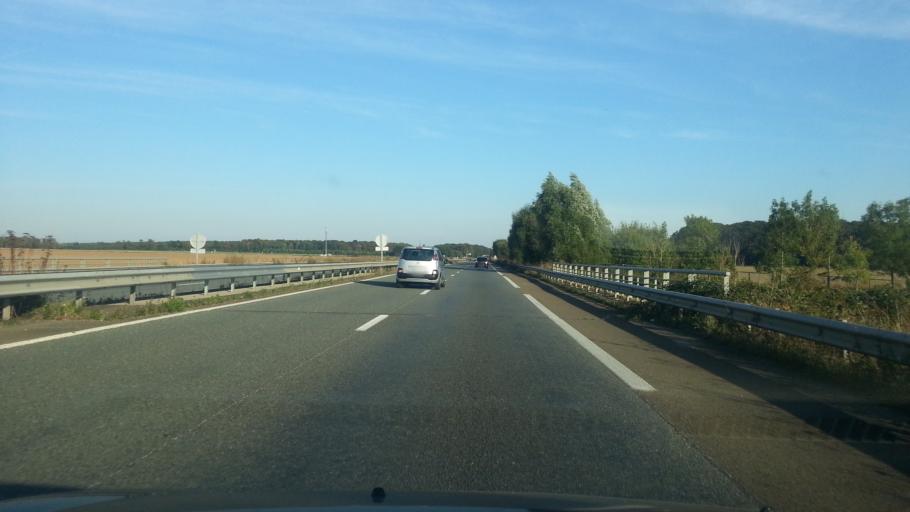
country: FR
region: Picardie
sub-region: Departement de l'Oise
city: Agnetz
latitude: 49.4111
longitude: 2.3292
